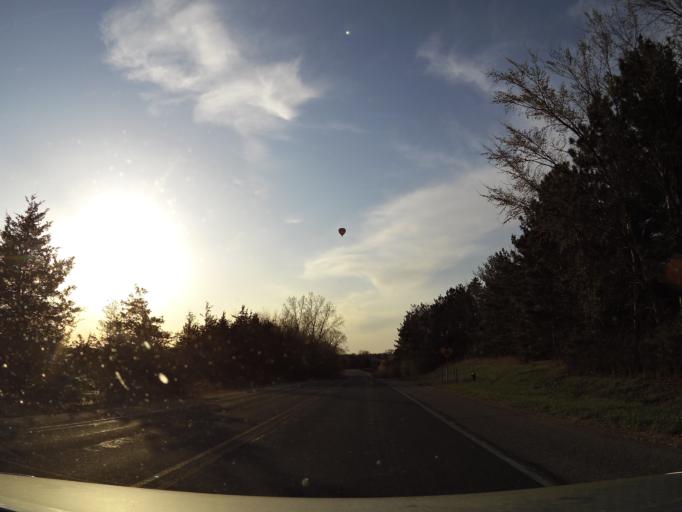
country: US
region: Minnesota
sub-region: Washington County
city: Lakeland
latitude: 44.9406
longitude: -92.7277
